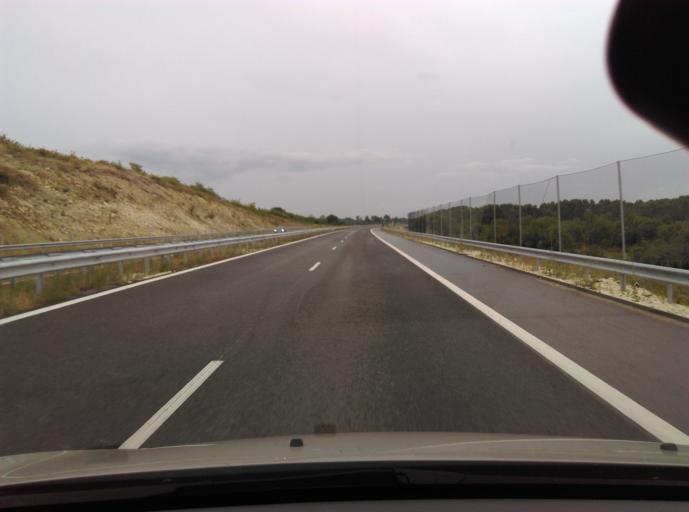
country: BG
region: Stara Zagora
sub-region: Obshtina Chirpan
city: Chirpan
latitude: 42.0953
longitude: 25.4386
